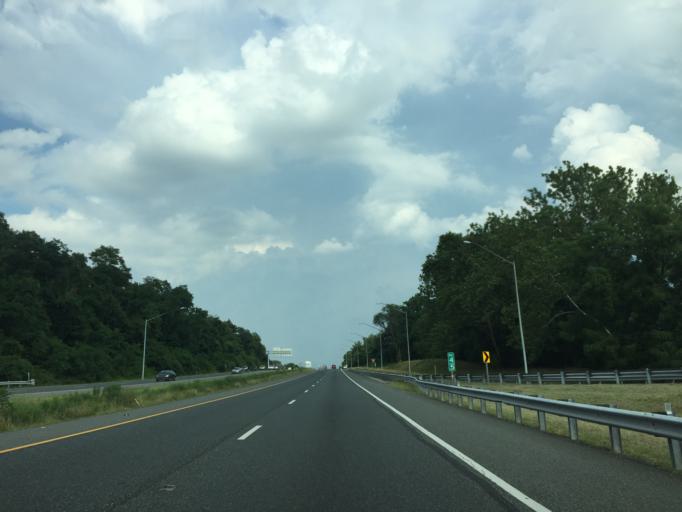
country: US
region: Maryland
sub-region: Baltimore County
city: Baltimore Highlands
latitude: 39.2319
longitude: -76.6494
